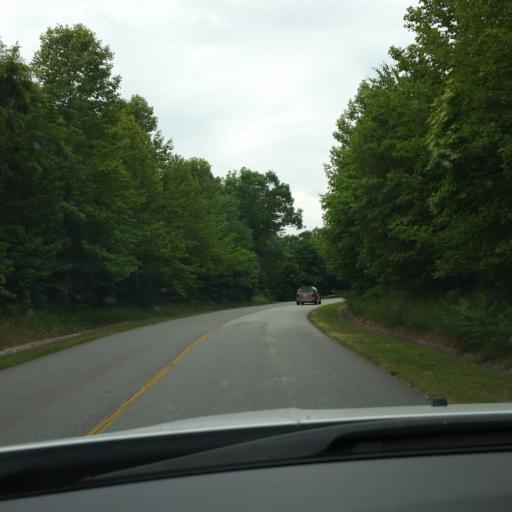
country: US
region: North Carolina
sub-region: Buncombe County
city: Biltmore Forest
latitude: 35.5677
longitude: -82.4852
